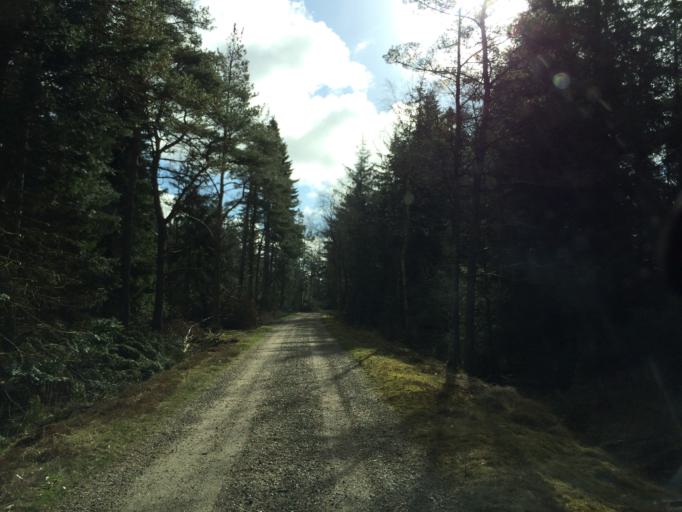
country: DK
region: Central Jutland
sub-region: Holstebro Kommune
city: Ulfborg
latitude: 56.2743
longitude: 8.4265
